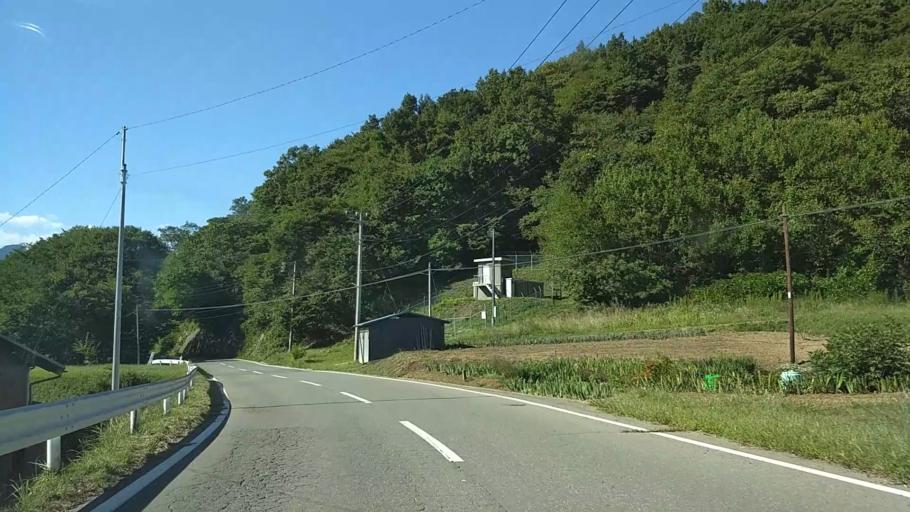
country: JP
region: Nagano
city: Nagano-shi
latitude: 36.6059
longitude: 138.0925
